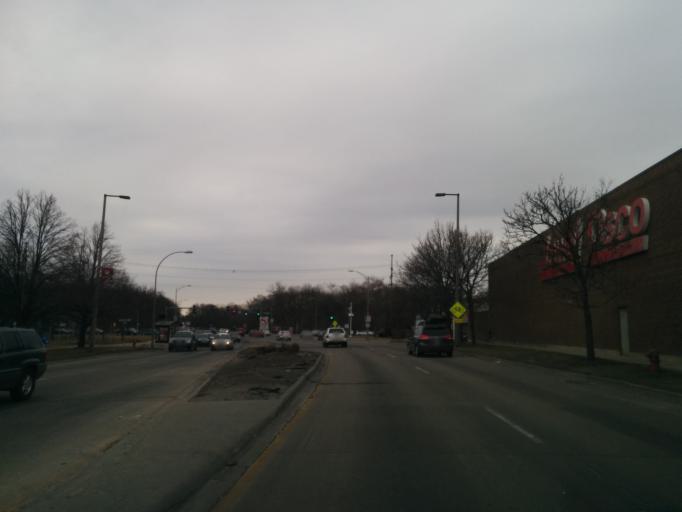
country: US
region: Illinois
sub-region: Cook County
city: Westchester
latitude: 41.8500
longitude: -87.8817
